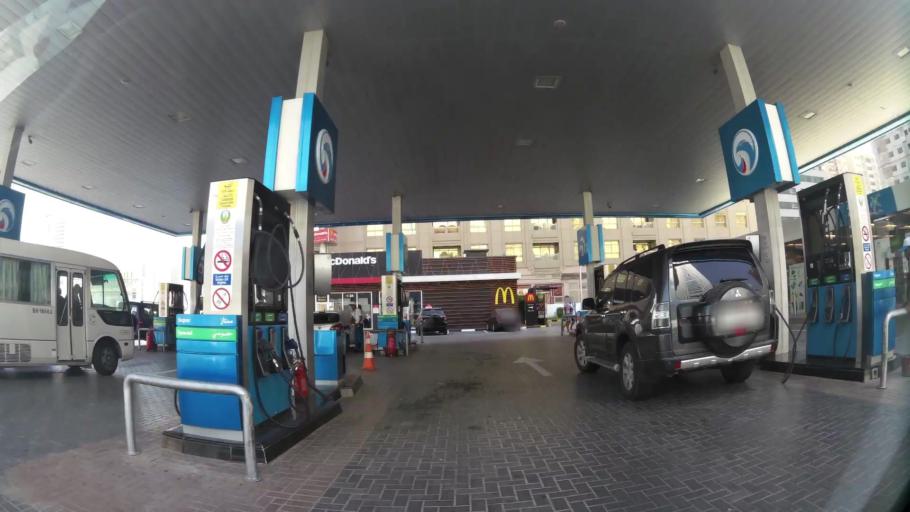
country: AE
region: Ash Shariqah
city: Sharjah
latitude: 25.3035
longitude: 55.3704
